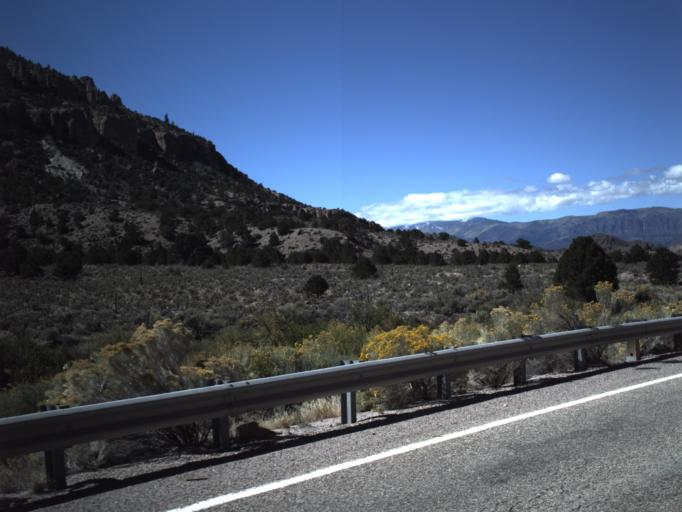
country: US
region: Utah
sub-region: Piute County
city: Junction
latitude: 38.1926
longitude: -112.1336
